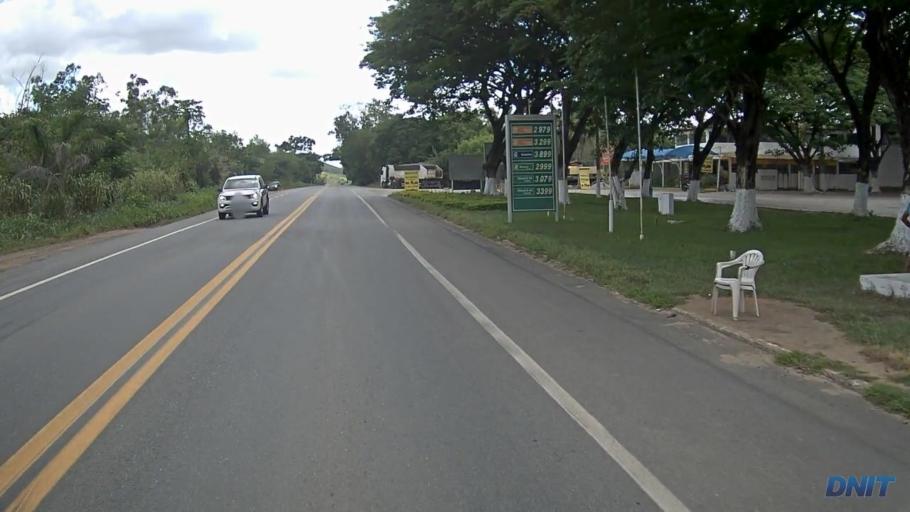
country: BR
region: Minas Gerais
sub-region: Governador Valadares
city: Governador Valadares
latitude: -18.9383
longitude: -42.0550
